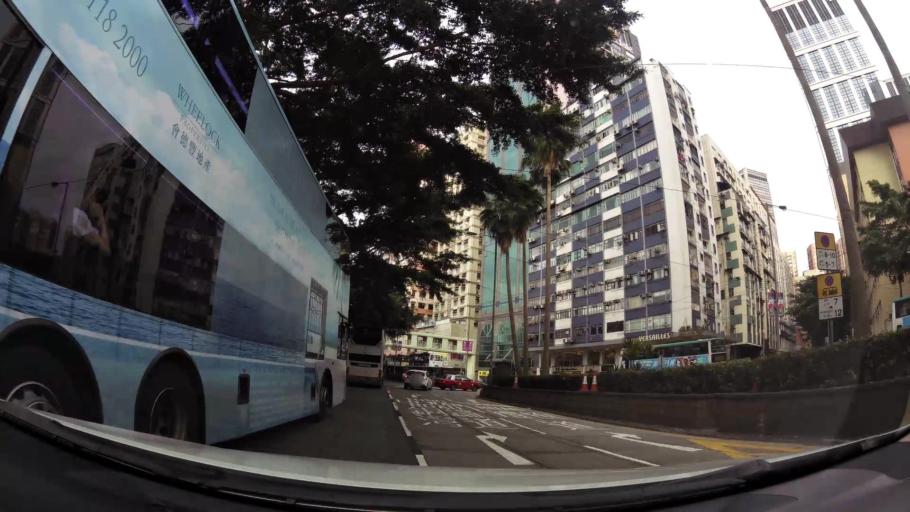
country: HK
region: Wanchai
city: Wan Chai
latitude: 22.2794
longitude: 114.1873
